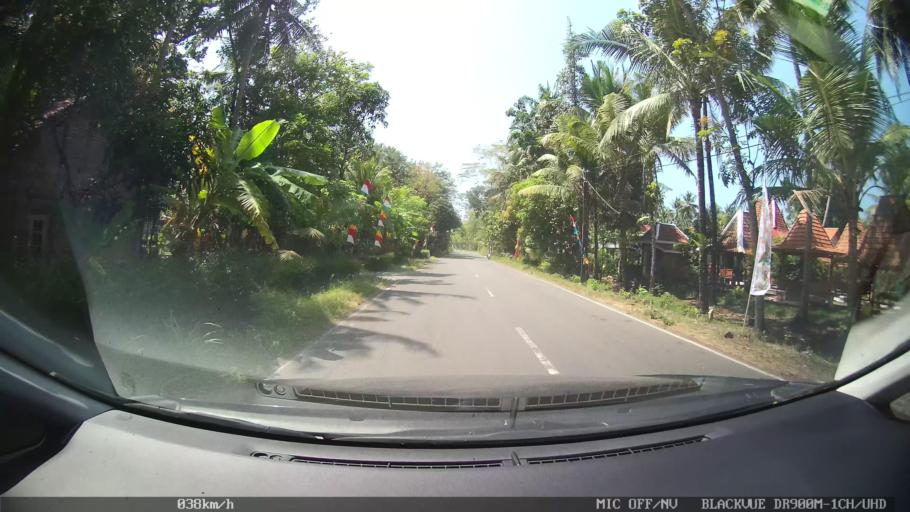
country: ID
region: Daerah Istimewa Yogyakarta
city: Srandakan
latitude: -7.8904
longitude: 110.0494
